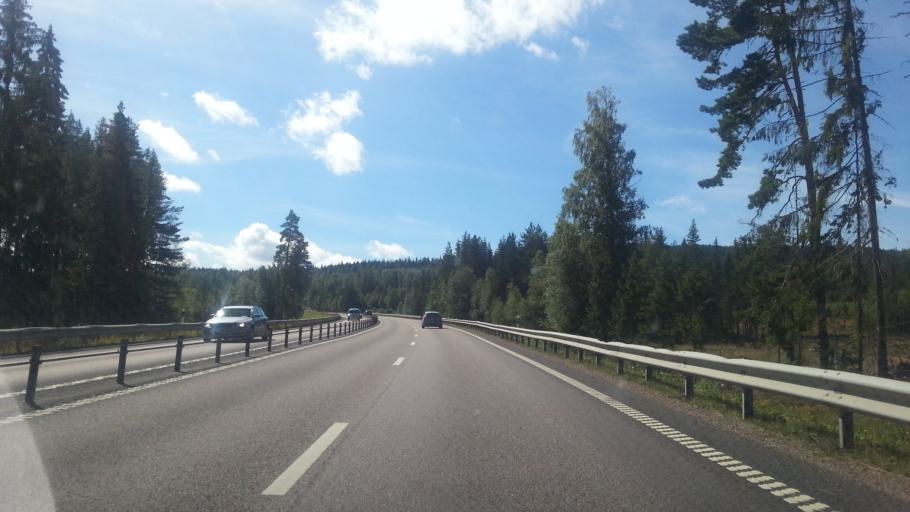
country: SE
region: Dalarna
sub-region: Borlange Kommun
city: Borlaenge
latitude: 60.3935
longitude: 15.3111
